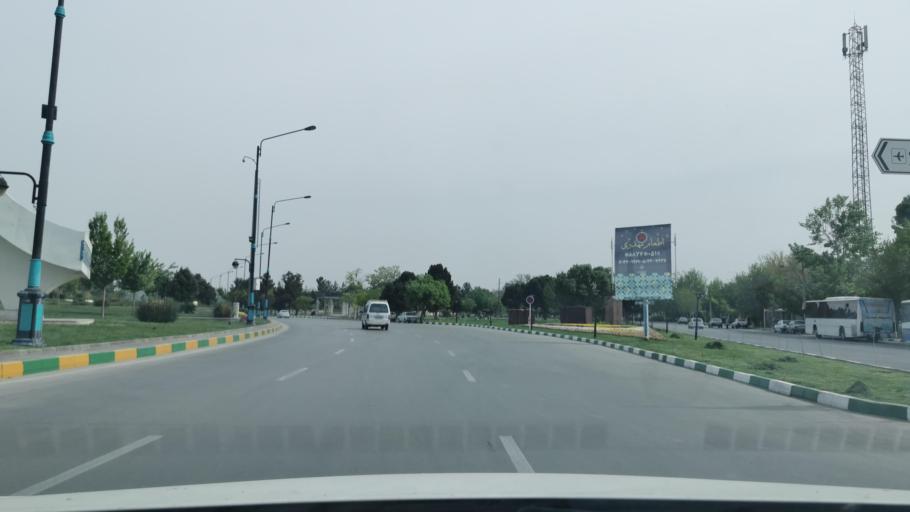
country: IR
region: Razavi Khorasan
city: Mashhad
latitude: 36.2443
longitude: 59.6221
